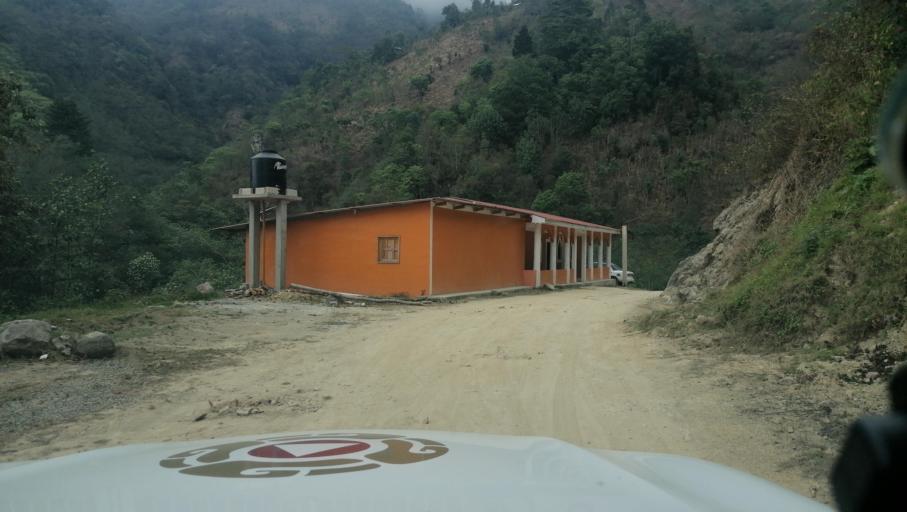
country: GT
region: San Marcos
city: Tacana
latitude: 15.2088
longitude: -92.1711
